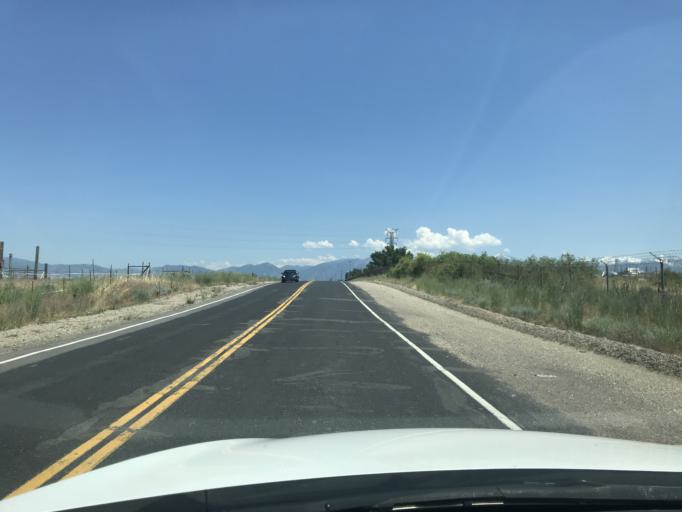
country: US
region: Utah
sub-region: Salt Lake County
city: Magna
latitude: 40.6820
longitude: -112.0865
